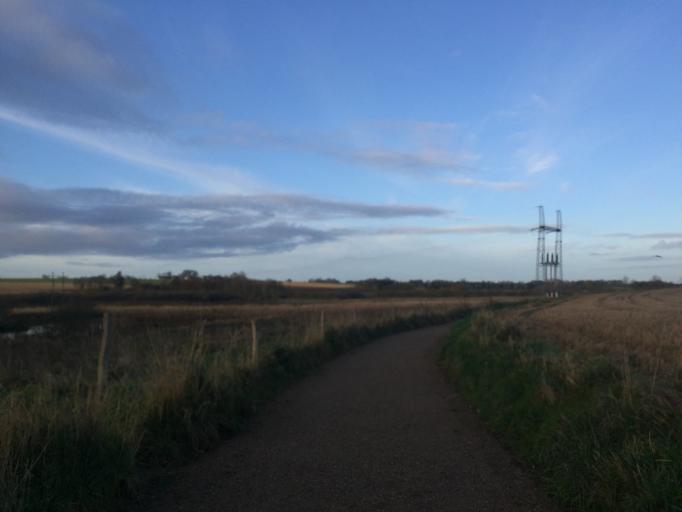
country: DK
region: Zealand
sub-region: Ringsted Kommune
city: Ringsted
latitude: 55.4524
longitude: 11.7665
